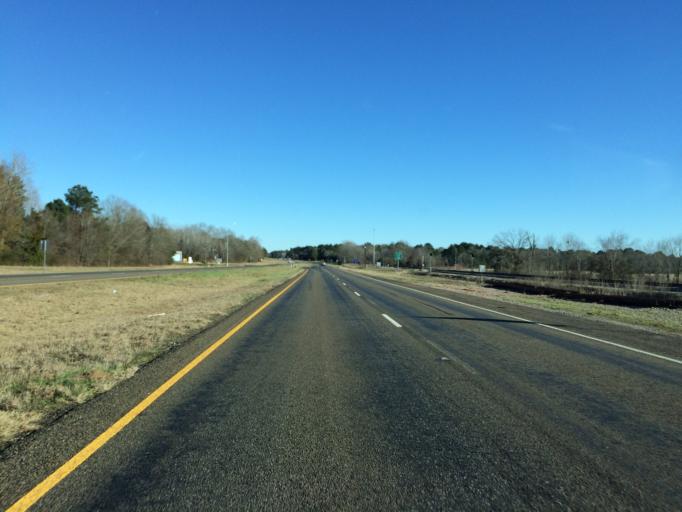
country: US
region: Texas
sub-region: Wood County
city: Hawkins
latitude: 32.6041
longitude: -95.2786
